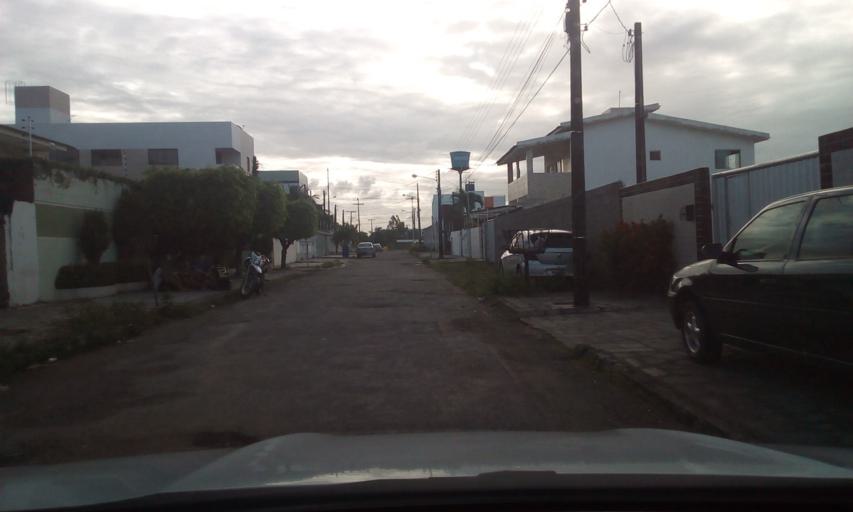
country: BR
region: Paraiba
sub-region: Joao Pessoa
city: Joao Pessoa
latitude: -7.1589
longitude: -34.8207
